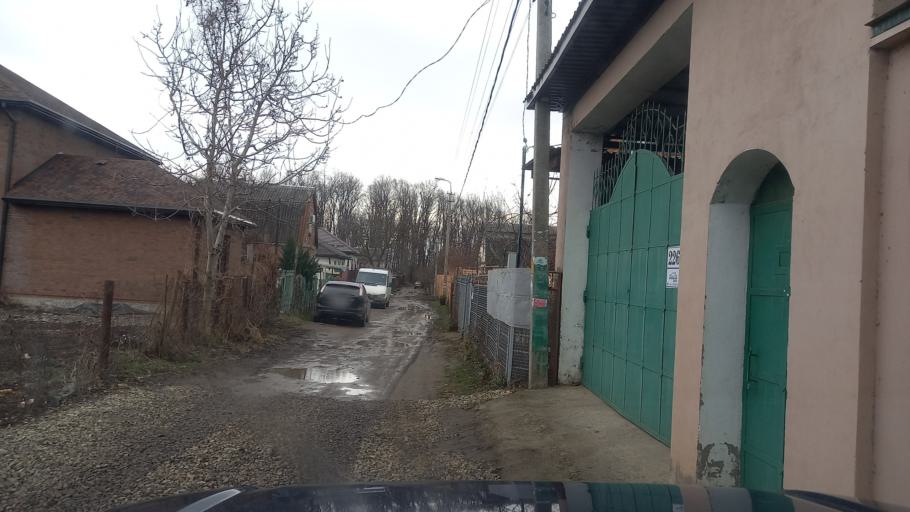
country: RU
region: Krasnodarskiy
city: Pashkovskiy
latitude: 45.0535
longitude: 39.1778
